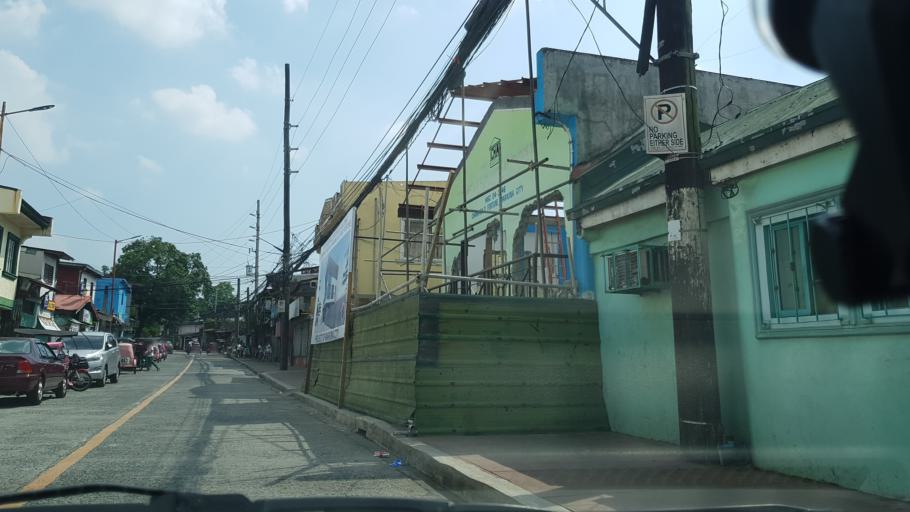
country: PH
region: Calabarzon
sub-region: Province of Rizal
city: Antipolo
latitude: 14.6601
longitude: 121.1282
